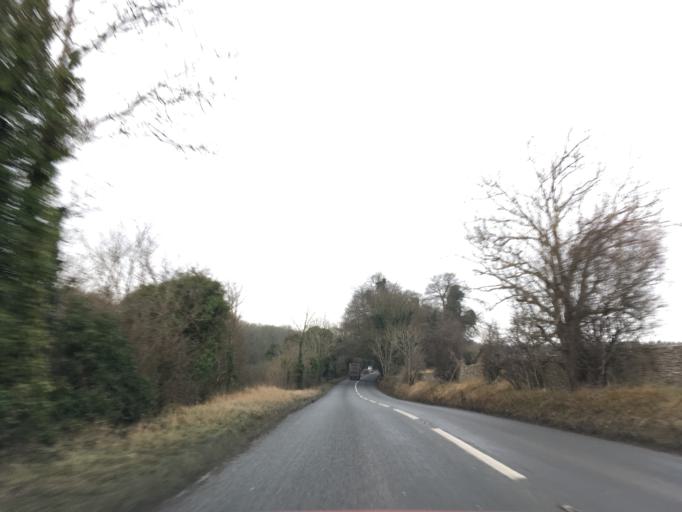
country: GB
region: England
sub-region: Gloucestershire
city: Coates
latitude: 51.6730
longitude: -2.0695
